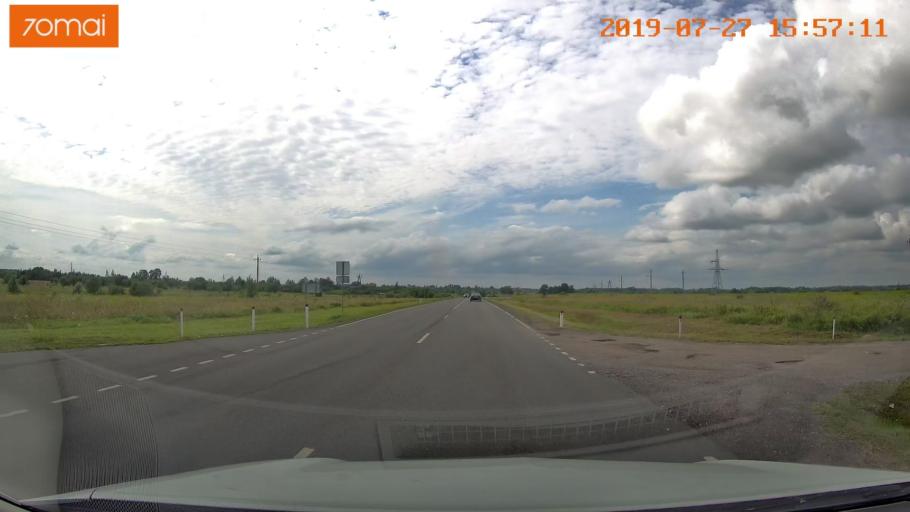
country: RU
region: Kaliningrad
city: Chernyakhovsk
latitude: 54.6224
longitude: 21.8884
